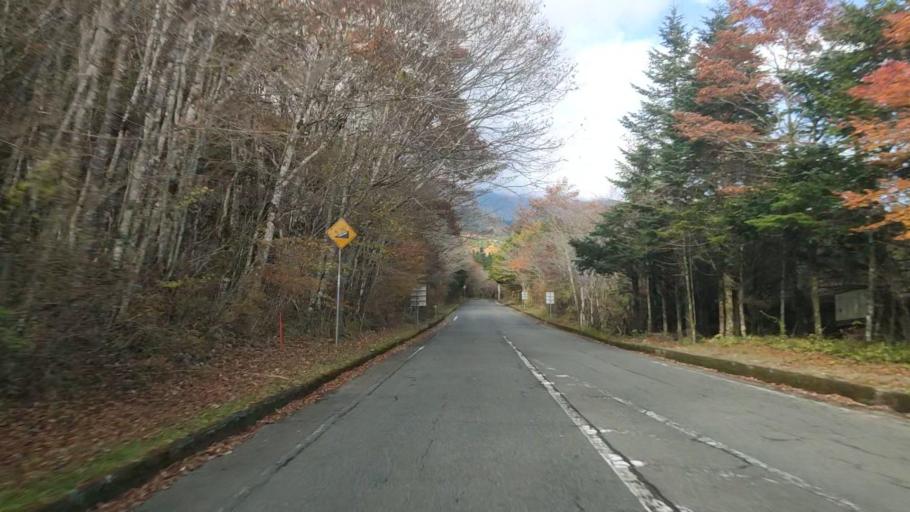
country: JP
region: Shizuoka
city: Fujinomiya
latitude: 35.2979
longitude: 138.7165
